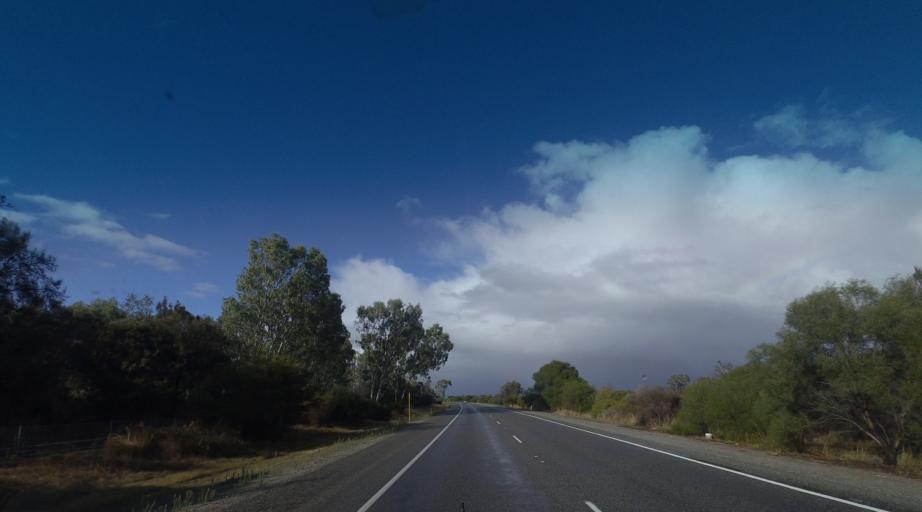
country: AU
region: Western Australia
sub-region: Armadale
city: Brookdale
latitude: -32.1680
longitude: 115.9610
